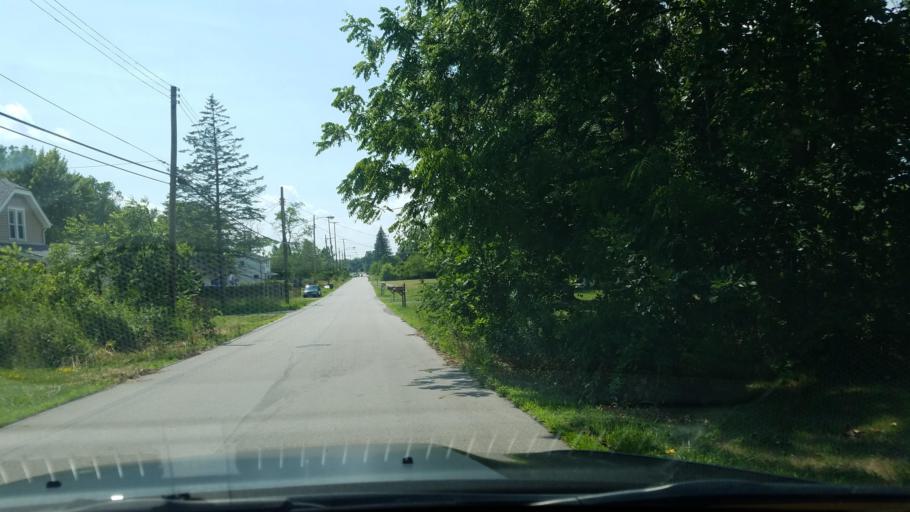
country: US
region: Ohio
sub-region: Trumbull County
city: Bolindale
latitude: 41.2138
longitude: -80.7856
